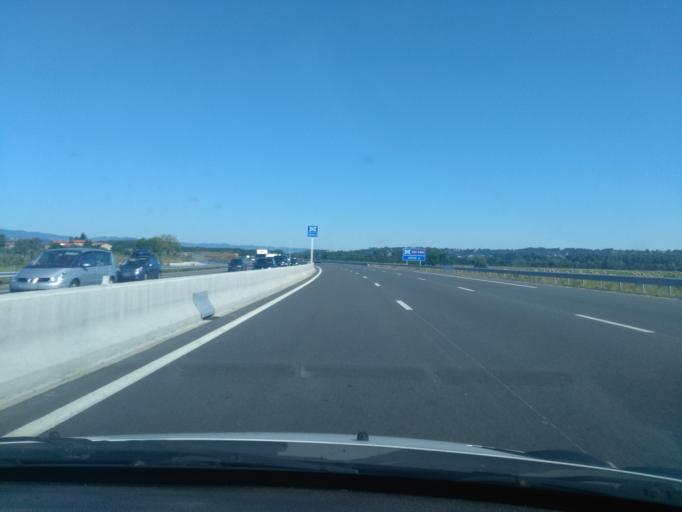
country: FR
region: Rhone-Alpes
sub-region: Departement du Rhone
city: Quincieux
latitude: 45.9126
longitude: 4.7946
